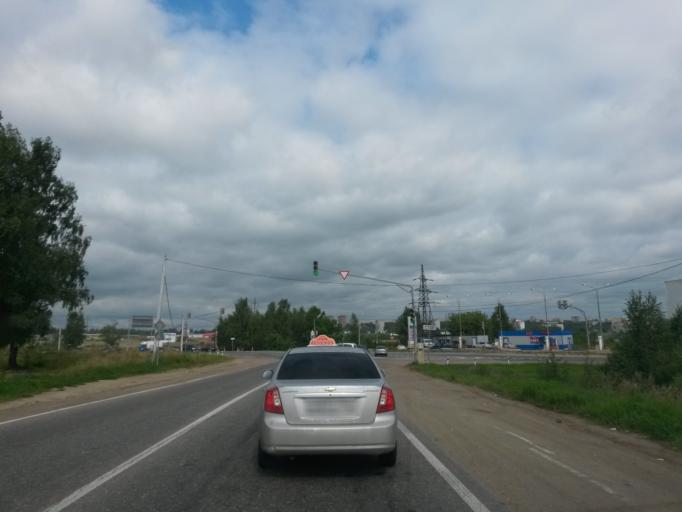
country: RU
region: Jaroslavl
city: Yaroslavl
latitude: 57.5581
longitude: 39.8576
